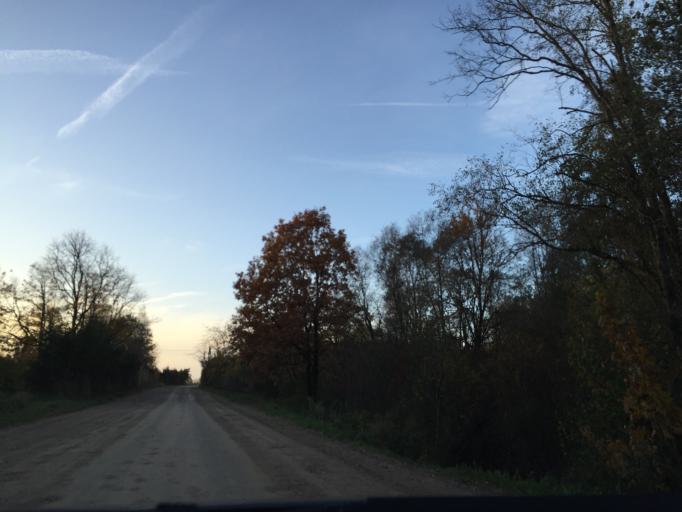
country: LV
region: Malpils
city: Malpils
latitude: 56.8833
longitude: 24.9683
